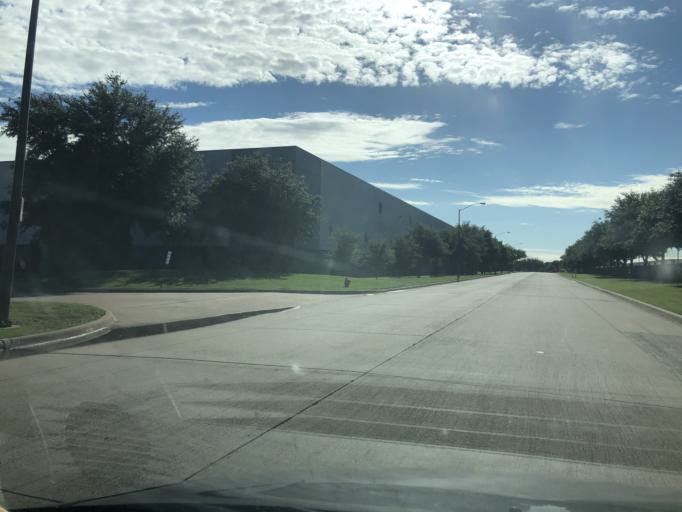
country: US
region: Texas
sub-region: Tarrant County
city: Euless
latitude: 32.8196
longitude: -97.0448
